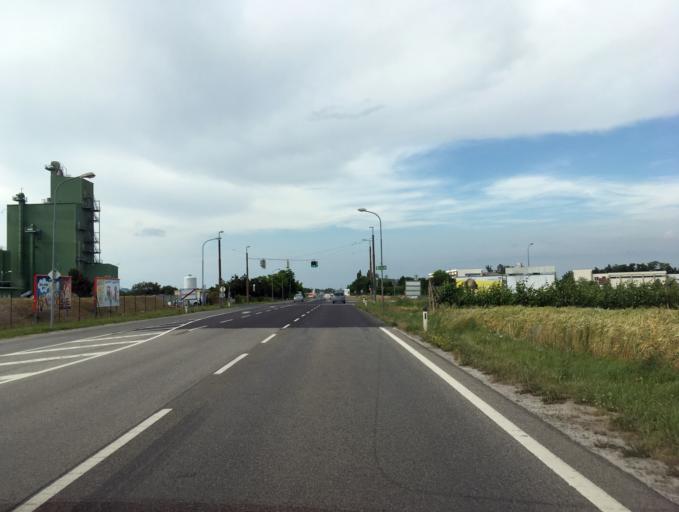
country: AT
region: Lower Austria
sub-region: Politischer Bezirk Baden
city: Traiskirchen
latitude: 47.9915
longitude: 16.2972
